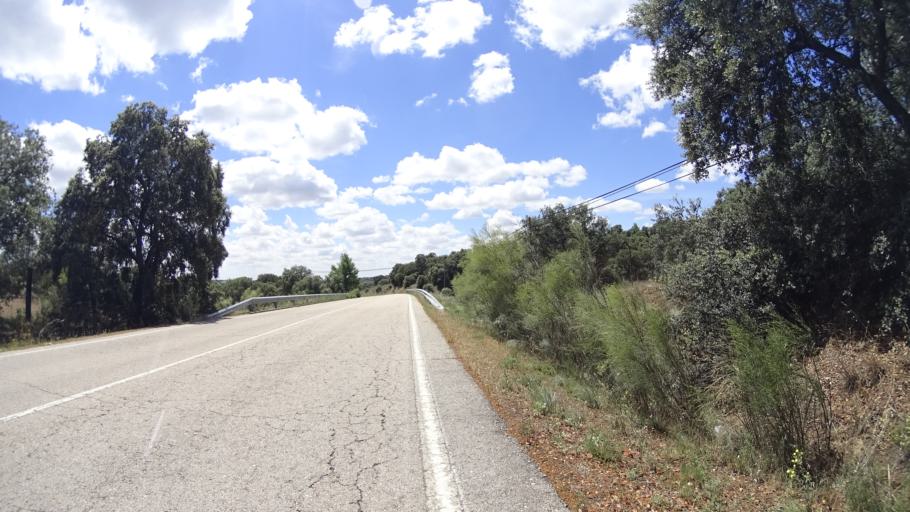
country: ES
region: Madrid
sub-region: Provincia de Madrid
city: Villanueva del Pardillo
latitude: 40.4480
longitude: -3.9536
